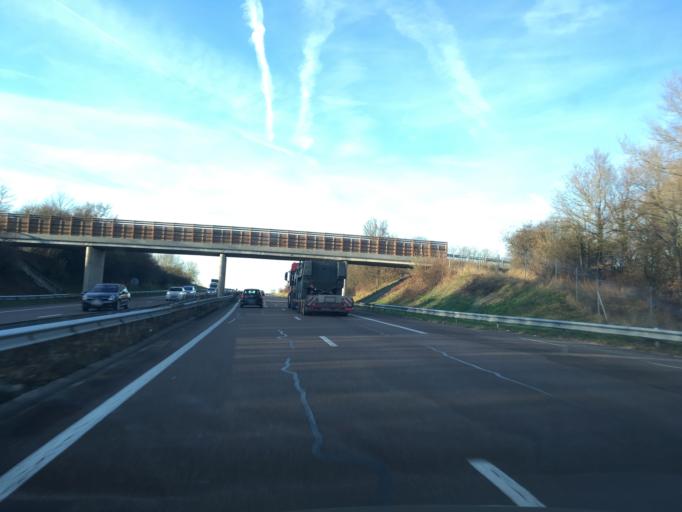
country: FR
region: Bourgogne
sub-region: Departement de l'Yonne
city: Avallon
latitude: 47.5588
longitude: 3.9483
